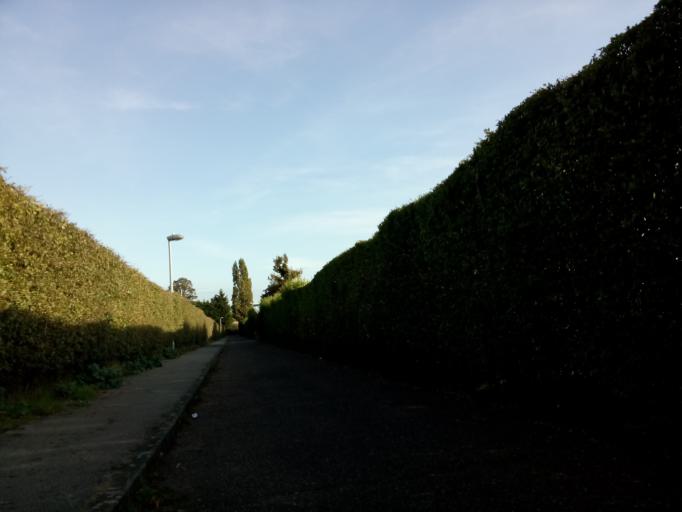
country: GB
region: England
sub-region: Suffolk
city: Ipswich
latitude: 52.0388
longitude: 1.1471
